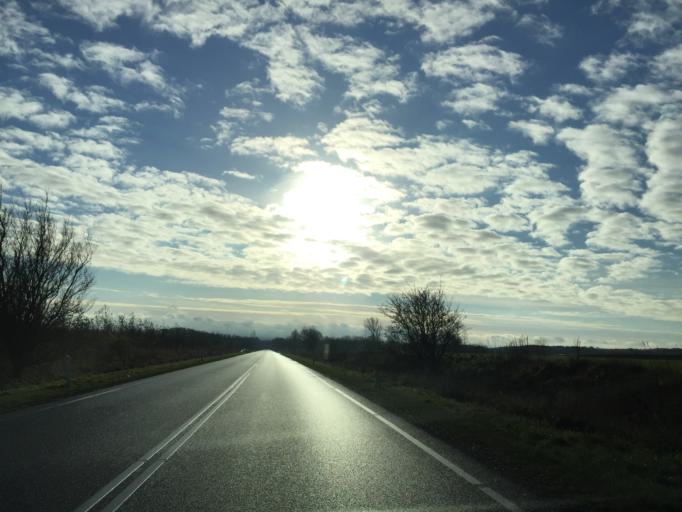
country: DK
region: Central Jutland
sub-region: Arhus Kommune
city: Sabro
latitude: 56.1942
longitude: 10.0095
